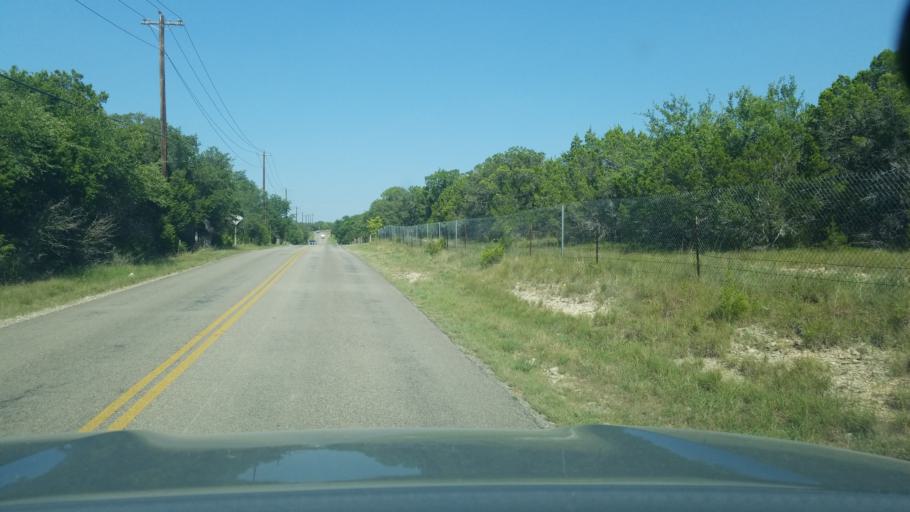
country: US
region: Texas
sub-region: Comal County
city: Bulverde
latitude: 29.7692
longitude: -98.5189
